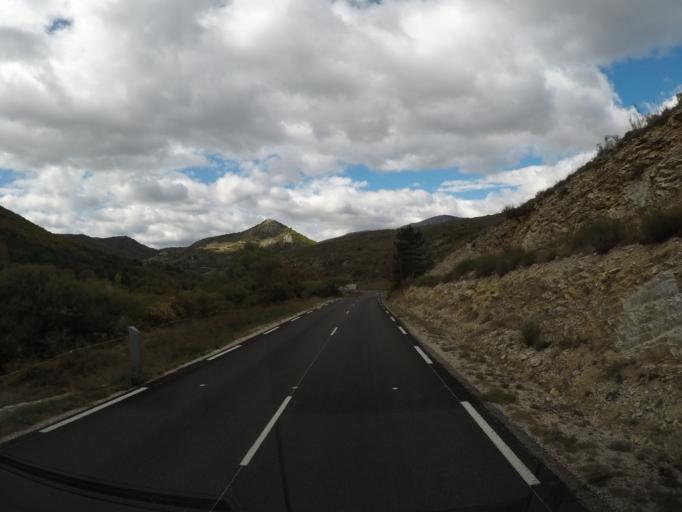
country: FR
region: Provence-Alpes-Cote d'Azur
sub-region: Departement du Vaucluse
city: Sault
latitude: 44.1854
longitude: 5.5490
